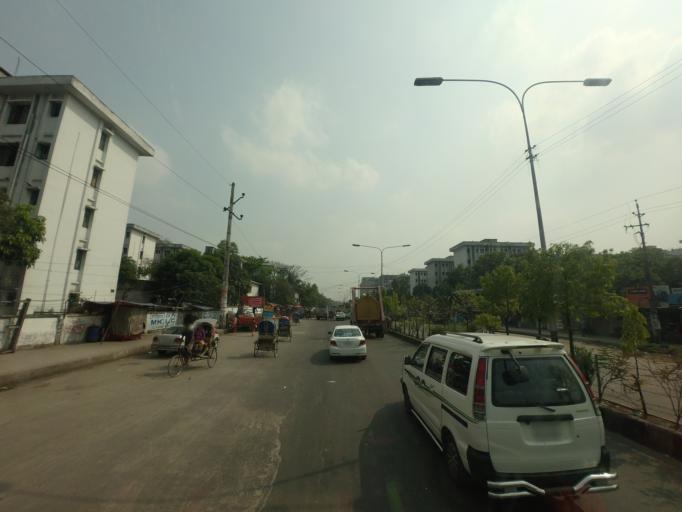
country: BD
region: Dhaka
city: Azimpur
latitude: 23.7918
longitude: 90.3538
